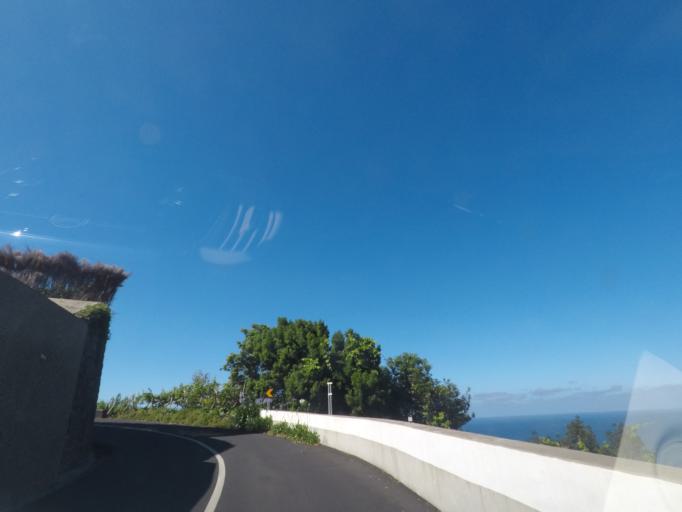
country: PT
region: Madeira
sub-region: Sao Vicente
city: Sao Vicente
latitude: 32.8194
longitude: -17.1037
